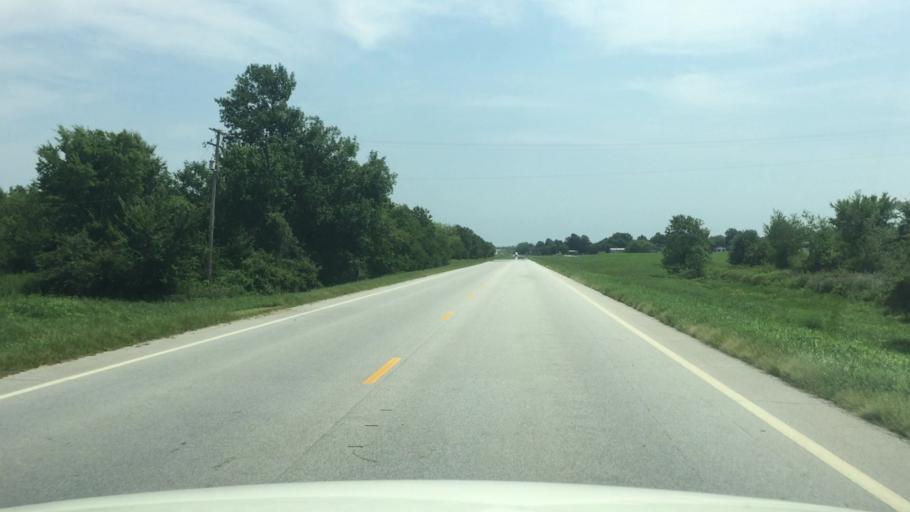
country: US
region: Kansas
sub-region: Cherokee County
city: Columbus
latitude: 37.1786
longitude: -94.8596
